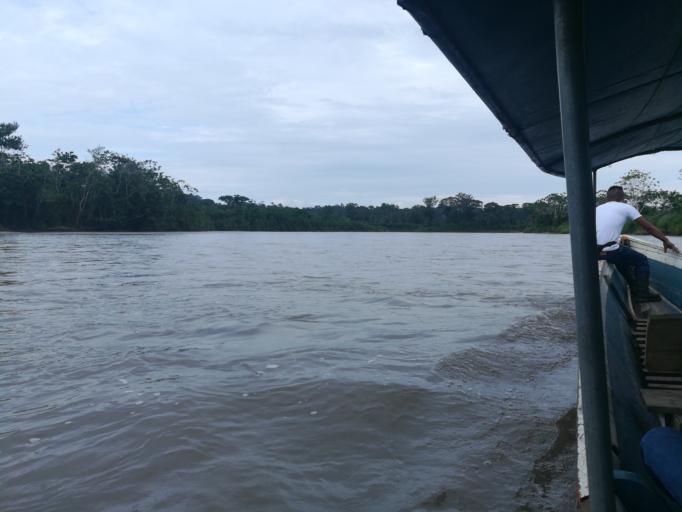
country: EC
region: Orellana
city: Boca Suno
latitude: -0.7583
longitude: -77.1535
